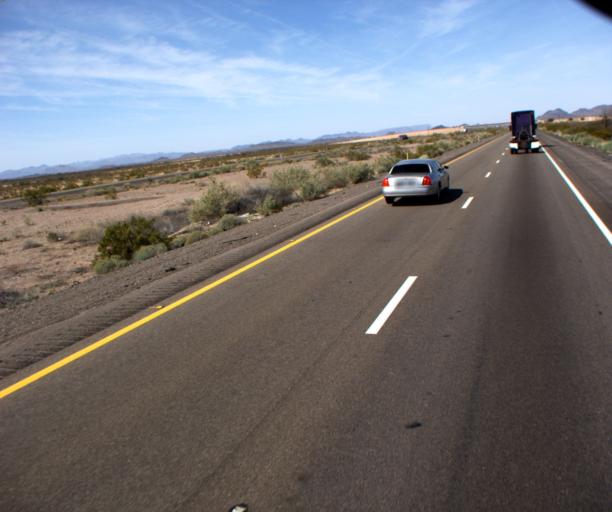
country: US
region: Arizona
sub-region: La Paz County
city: Salome
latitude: 33.5940
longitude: -113.5168
